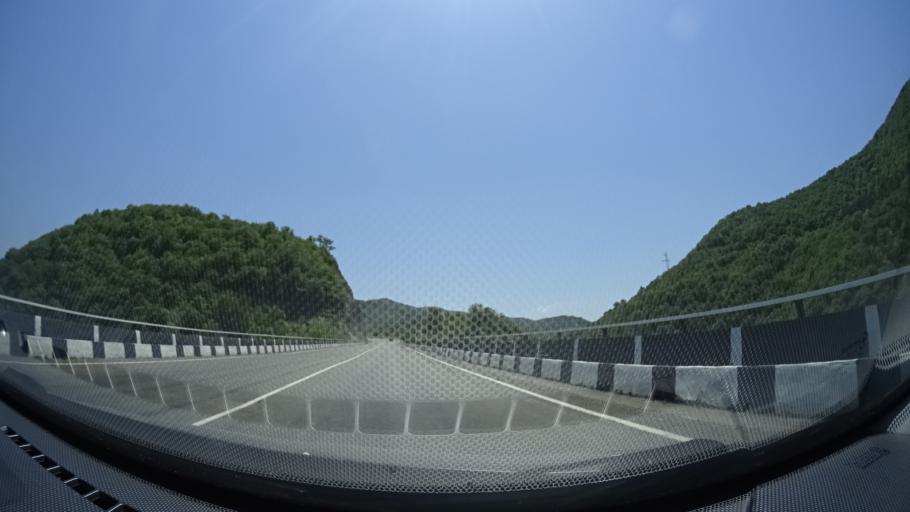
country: GE
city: Zhinvali
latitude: 42.1626
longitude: 44.7021
